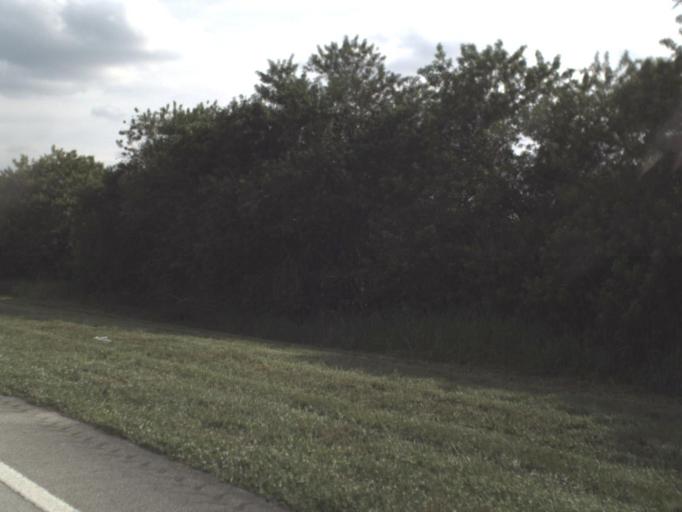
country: US
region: Florida
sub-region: Okeechobee County
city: Taylor Creek
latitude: 27.1828
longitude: -80.7133
